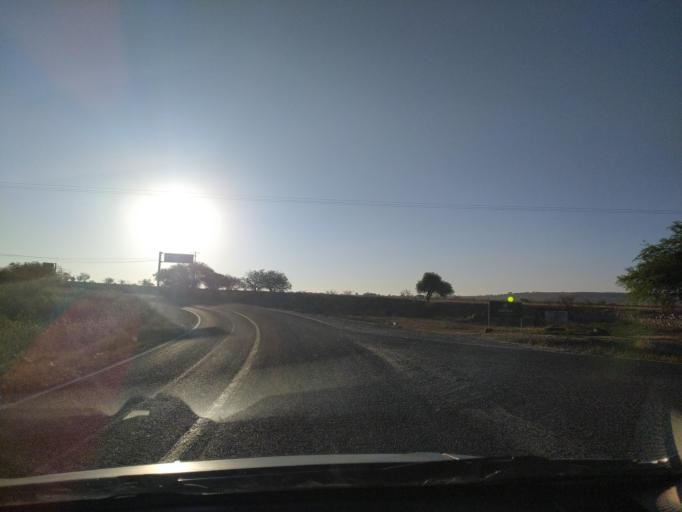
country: MX
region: Guanajuato
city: Ciudad Manuel Doblado
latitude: 20.7326
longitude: -101.8308
